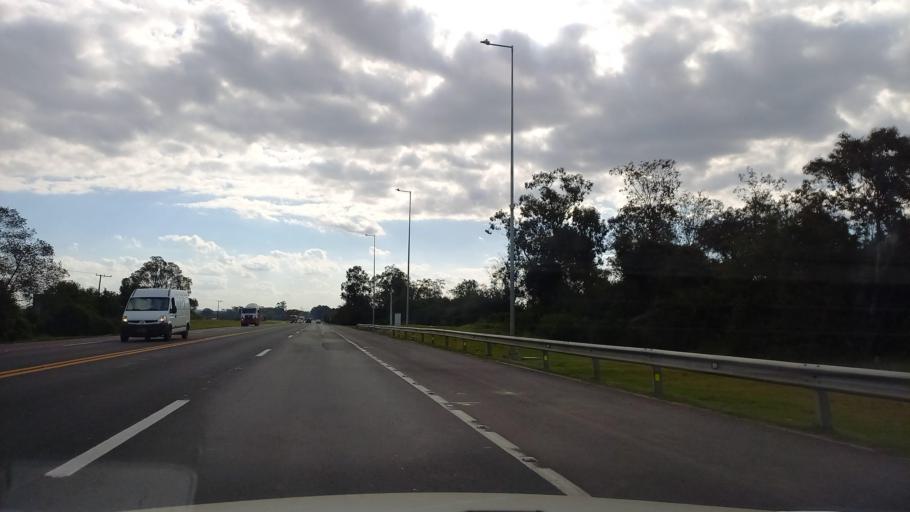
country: BR
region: Rio Grande do Sul
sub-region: Esteio
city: Esteio
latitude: -29.8354
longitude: -51.3101
